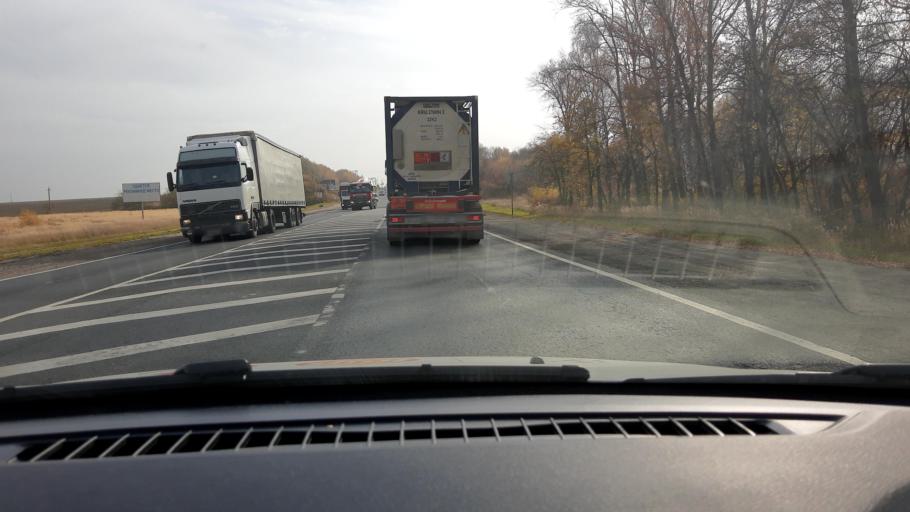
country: RU
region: Nizjnij Novgorod
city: Kstovo
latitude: 56.1201
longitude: 44.2730
